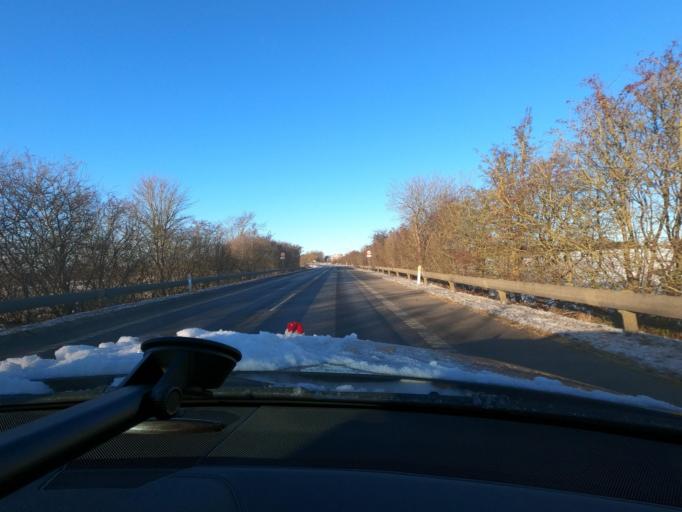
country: DK
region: South Denmark
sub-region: Sonderborg Kommune
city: Horuphav
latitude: 54.8931
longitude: 9.9698
